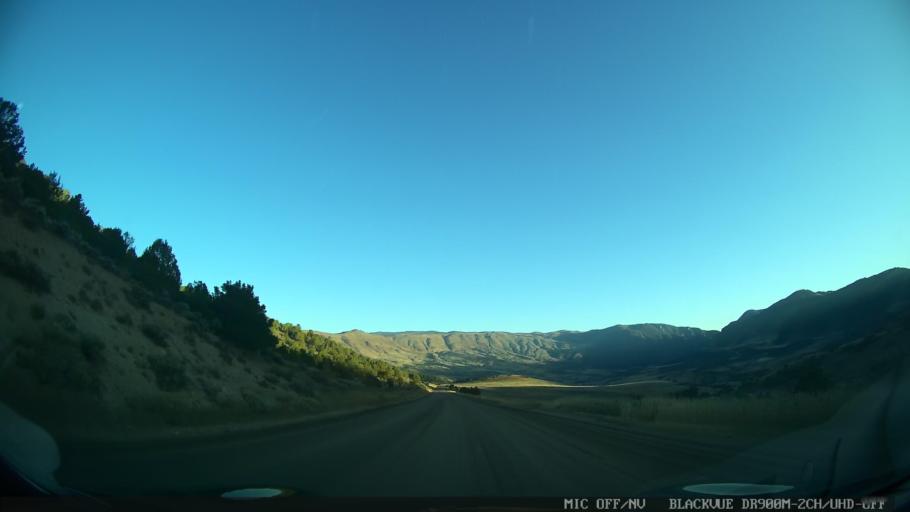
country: US
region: Colorado
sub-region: Grand County
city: Kremmling
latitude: 39.9565
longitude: -106.5193
